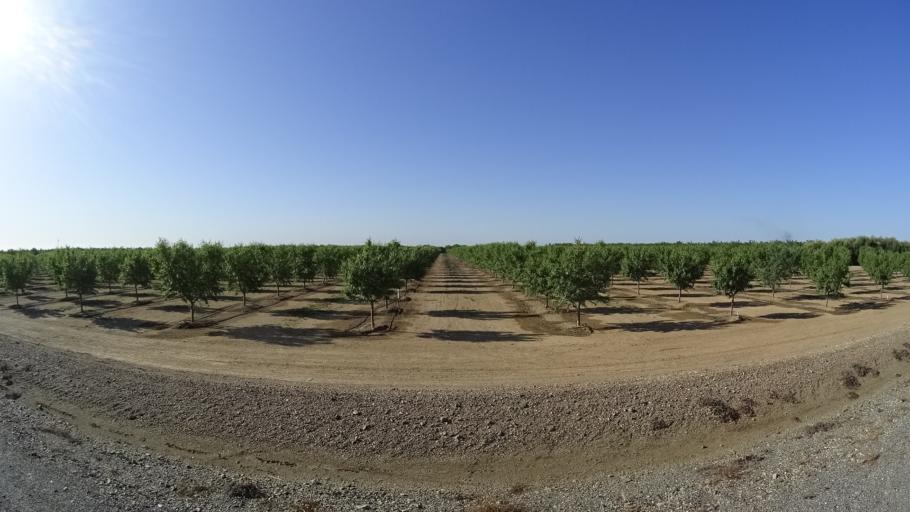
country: US
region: California
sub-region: Glenn County
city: Orland
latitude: 39.6815
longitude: -122.1342
